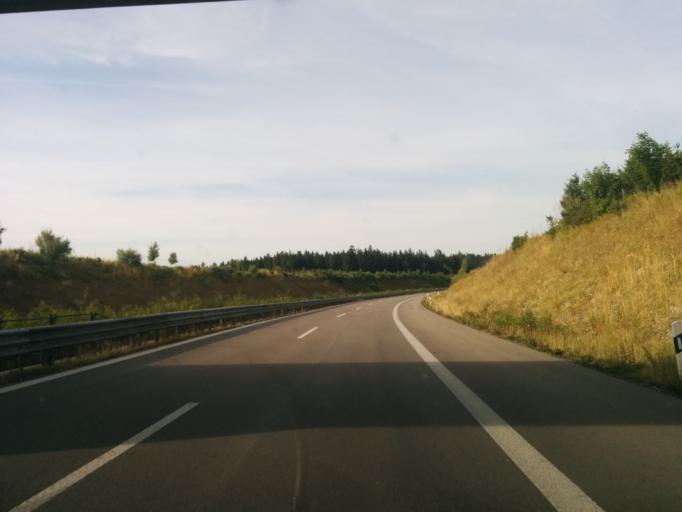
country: DE
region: Bavaria
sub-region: Upper Bavaria
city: Hurlach
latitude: 48.0896
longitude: 10.8378
